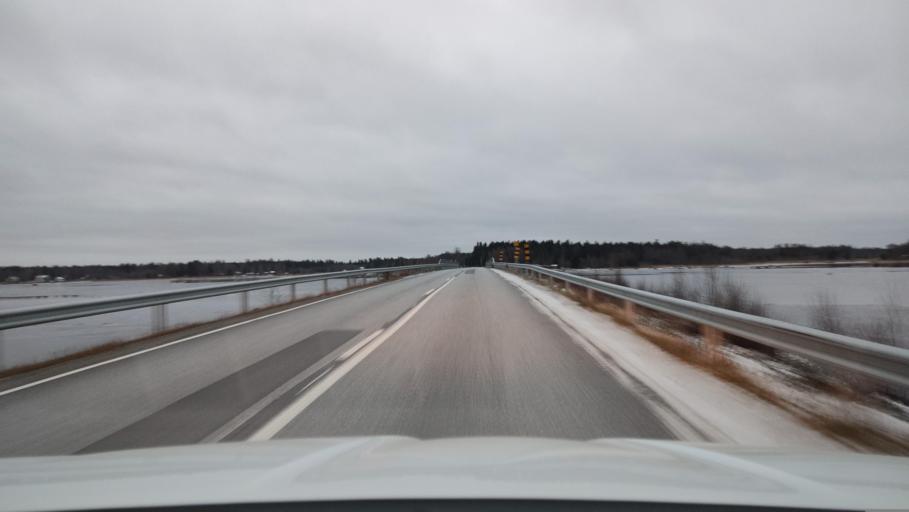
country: FI
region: Ostrobothnia
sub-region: Vaasa
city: Replot
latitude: 63.2753
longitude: 21.3439
